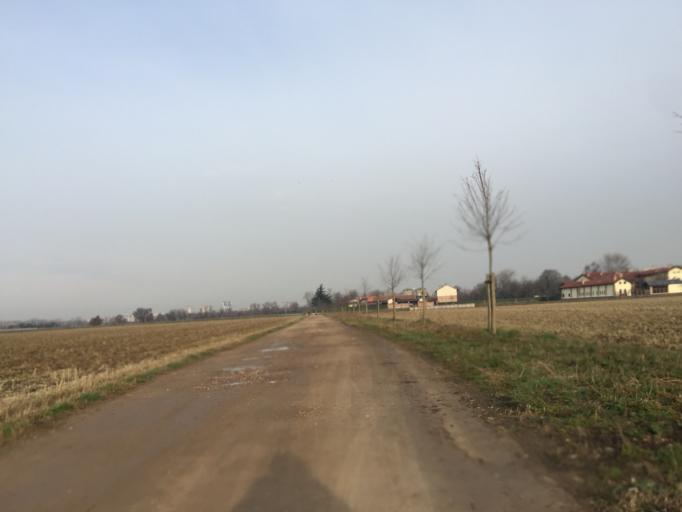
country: IT
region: Lombardy
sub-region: Citta metropolitana di Milano
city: Assago
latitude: 45.4273
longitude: 9.1460
